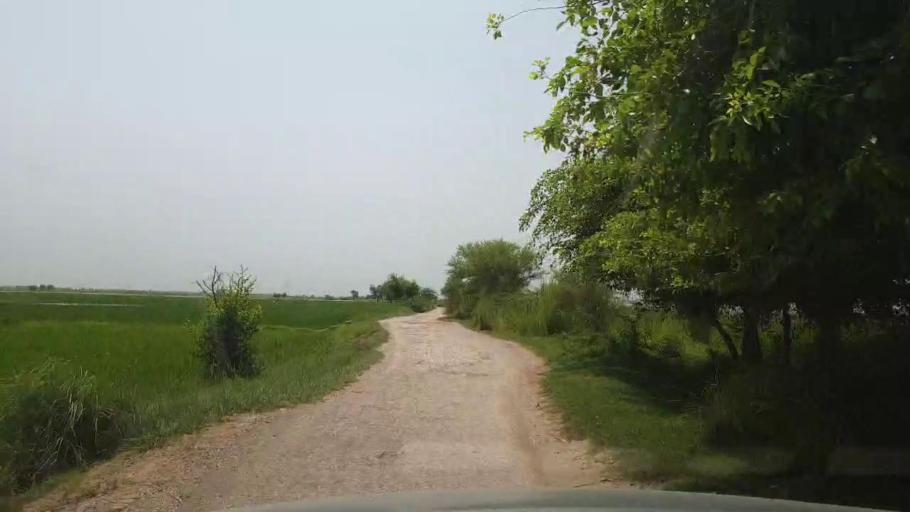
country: PK
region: Sindh
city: Garhi Yasin
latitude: 27.8733
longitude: 68.5009
